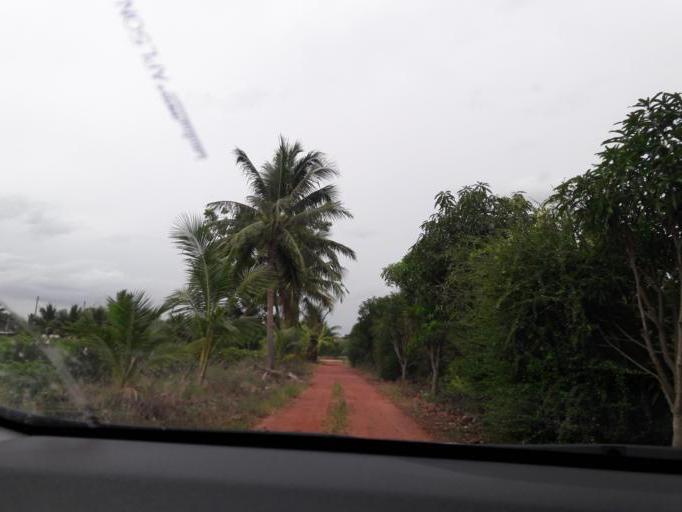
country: TH
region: Ratchaburi
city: Damnoen Saduak
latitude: 13.5418
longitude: 100.0371
